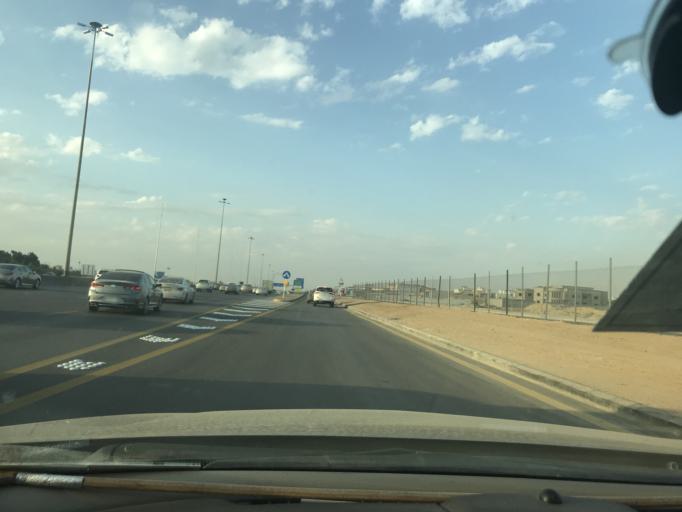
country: SA
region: Ar Riyad
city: Riyadh
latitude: 24.7443
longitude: 46.5860
